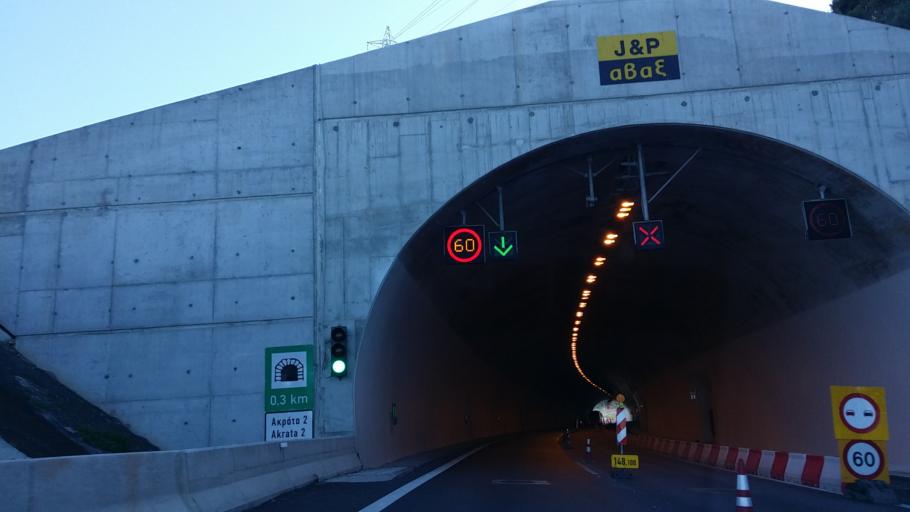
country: GR
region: West Greece
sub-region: Nomos Achaias
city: Aiyira
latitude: 38.1513
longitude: 22.3464
